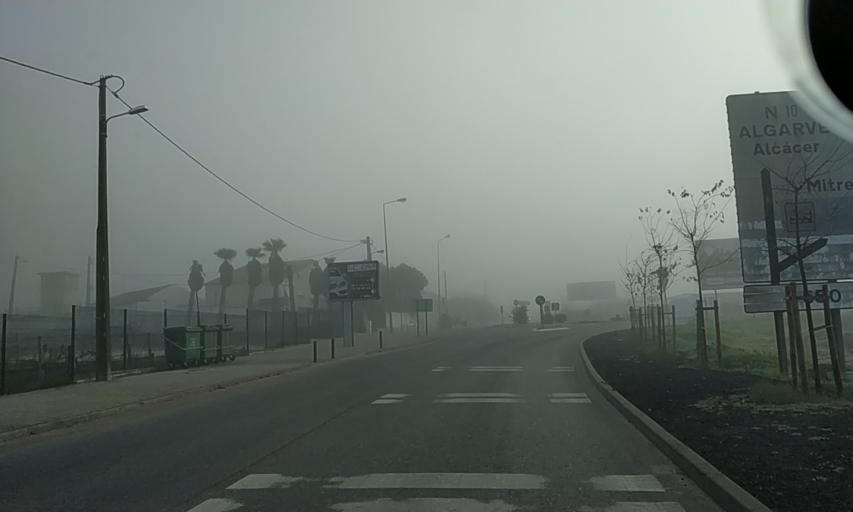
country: PT
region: Setubal
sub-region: Setubal
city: Setubal
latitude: 38.5376
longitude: -8.8527
